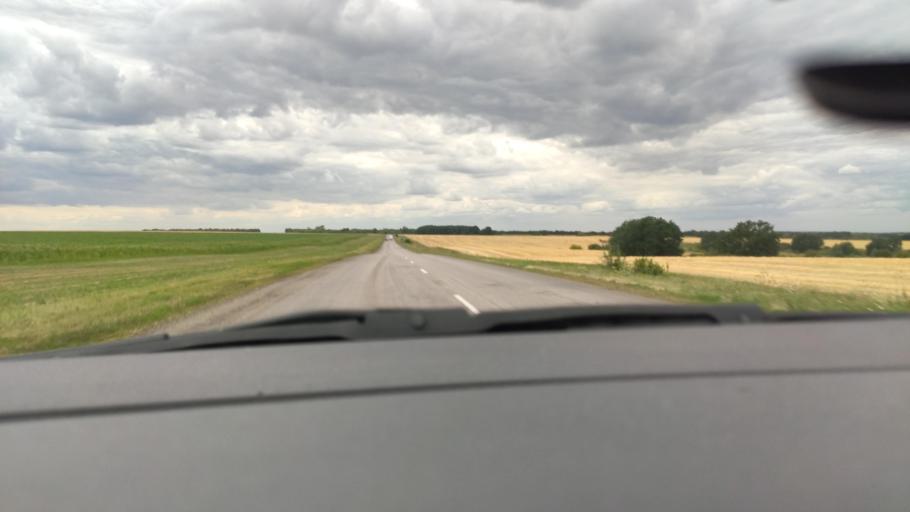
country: RU
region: Voronezj
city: Podgornoye
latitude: 51.9431
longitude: 39.0052
